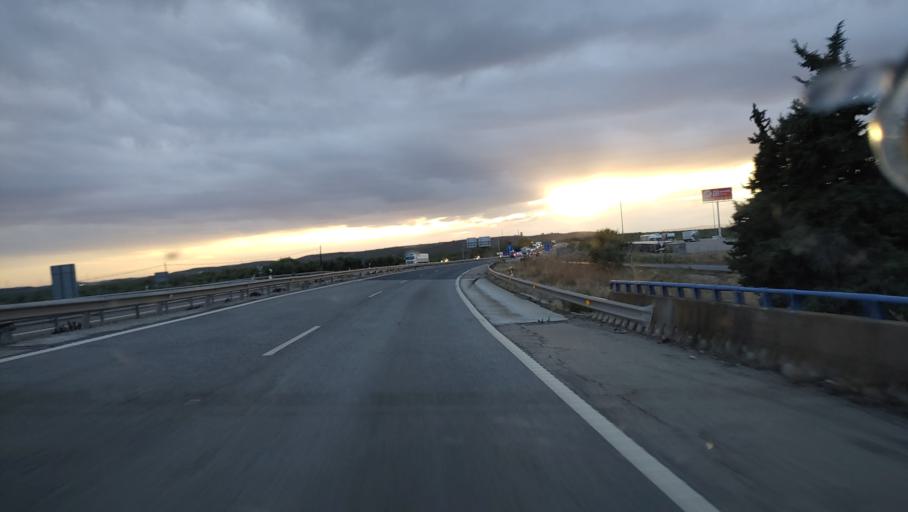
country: ES
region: Andalusia
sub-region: Provincia de Jaen
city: Guarroman
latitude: 38.1435
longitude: -3.7264
